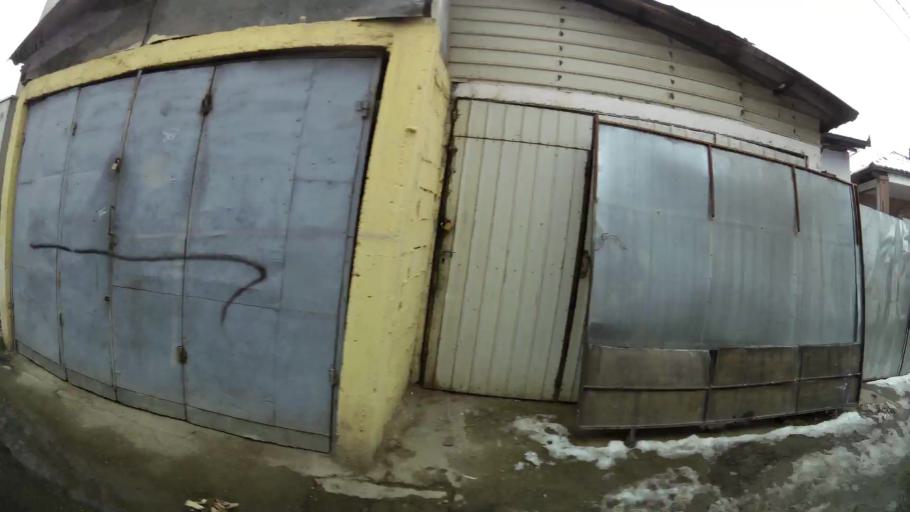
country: MK
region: Suto Orizari
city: Suto Orizare
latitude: 42.0455
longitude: 21.4248
